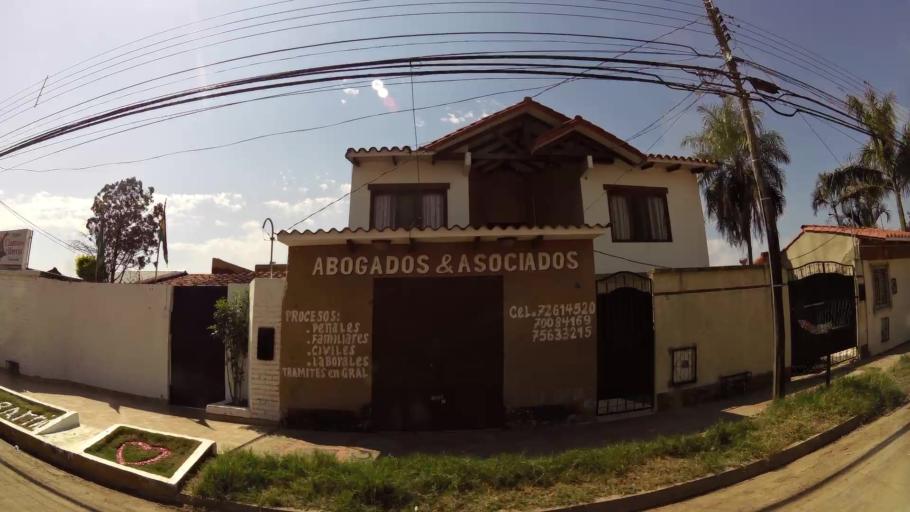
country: BO
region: Santa Cruz
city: Santa Cruz de la Sierra
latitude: -17.7344
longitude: -63.1475
